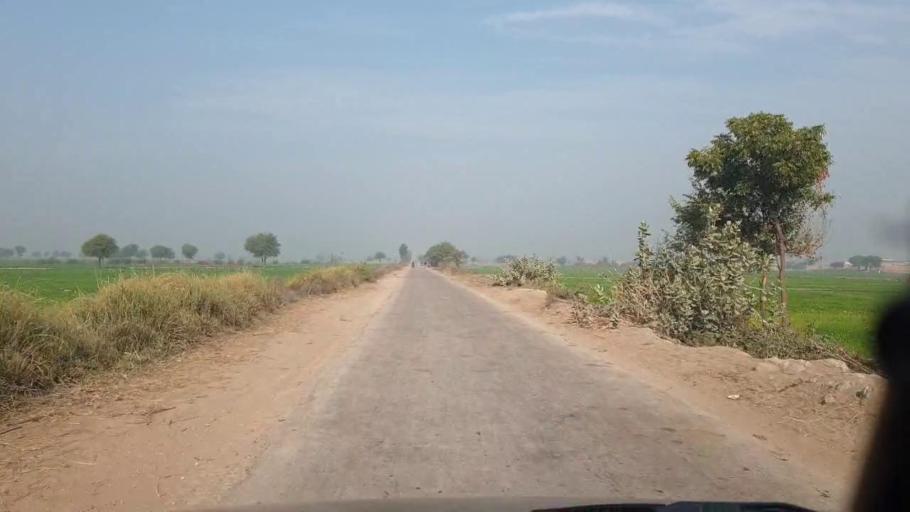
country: PK
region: Sindh
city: Shahdadpur
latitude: 25.9687
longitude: 68.5804
